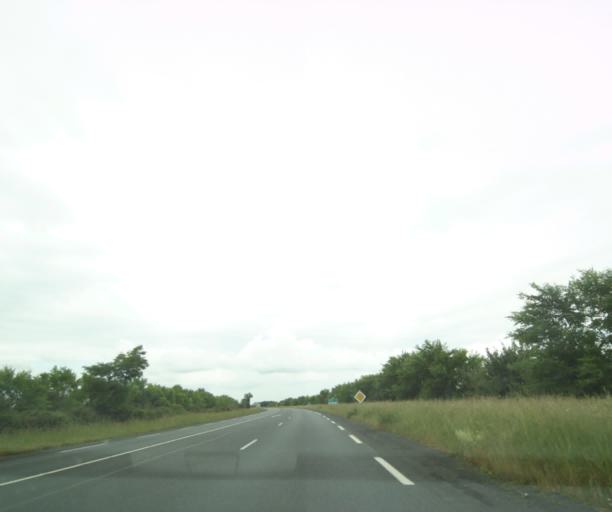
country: FR
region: Poitou-Charentes
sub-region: Departement des Deux-Sevres
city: Saint-Varent
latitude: 46.8718
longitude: -0.1986
